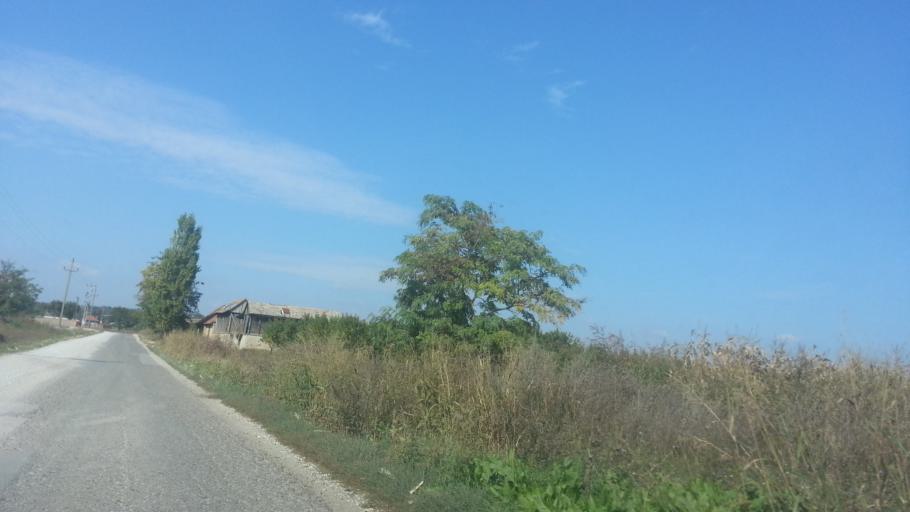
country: RS
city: Novi Slankamen
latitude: 45.1305
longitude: 20.2560
